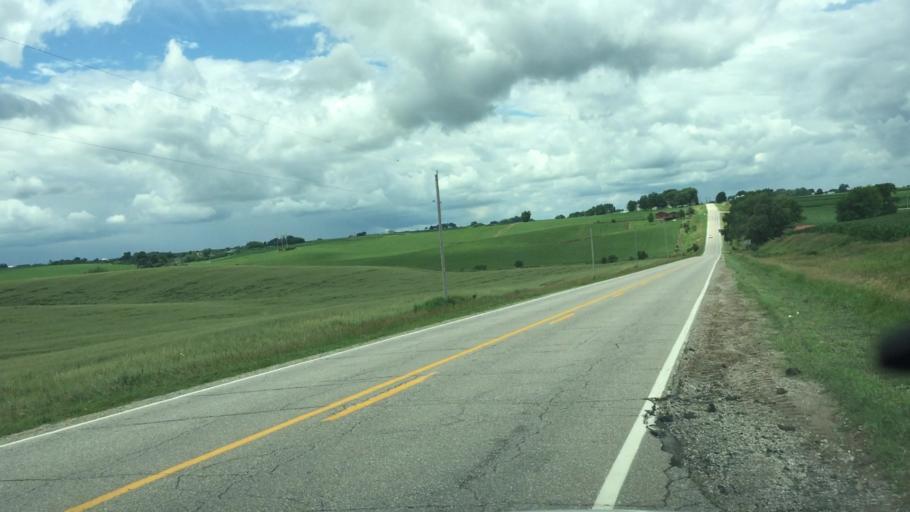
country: US
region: Iowa
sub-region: Jasper County
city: Monroe
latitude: 41.5736
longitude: -93.0738
